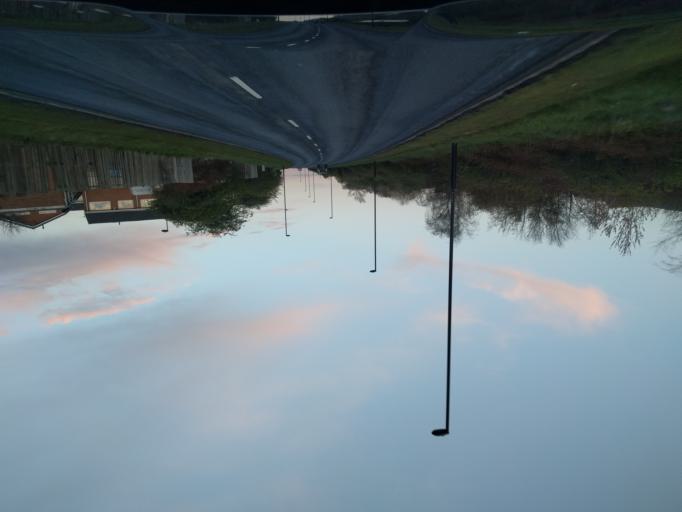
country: GB
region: England
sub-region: Northumberland
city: Seghill
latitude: 55.0413
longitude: -1.5703
